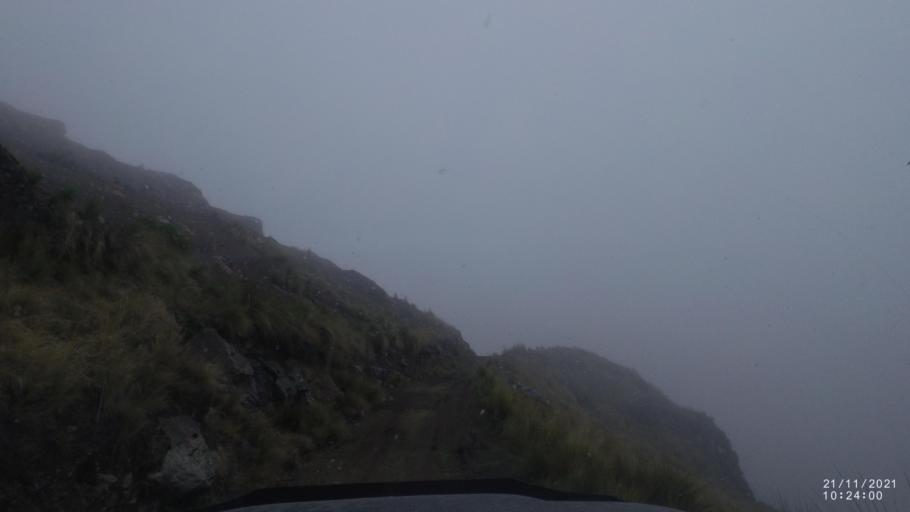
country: BO
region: Cochabamba
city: Cochabamba
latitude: -16.9804
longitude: -66.2629
